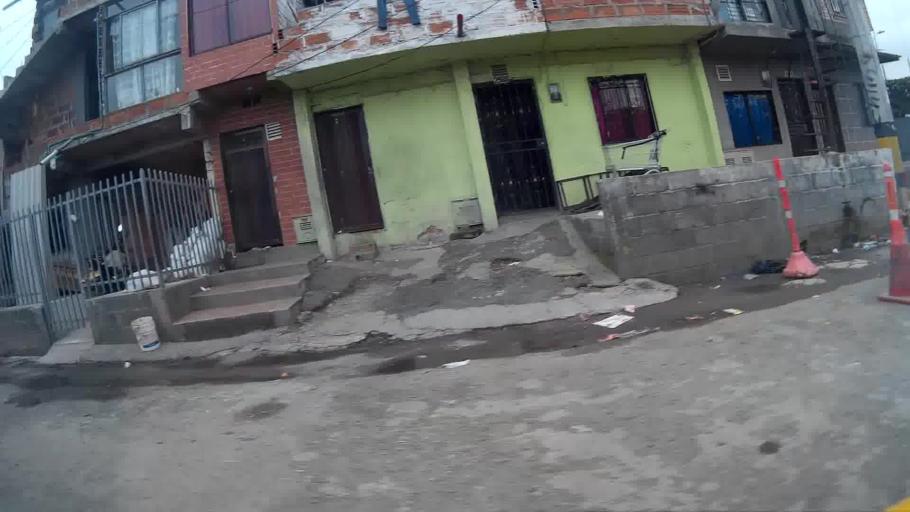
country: CO
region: Antioquia
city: Medellin
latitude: 6.2259
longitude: -75.5876
